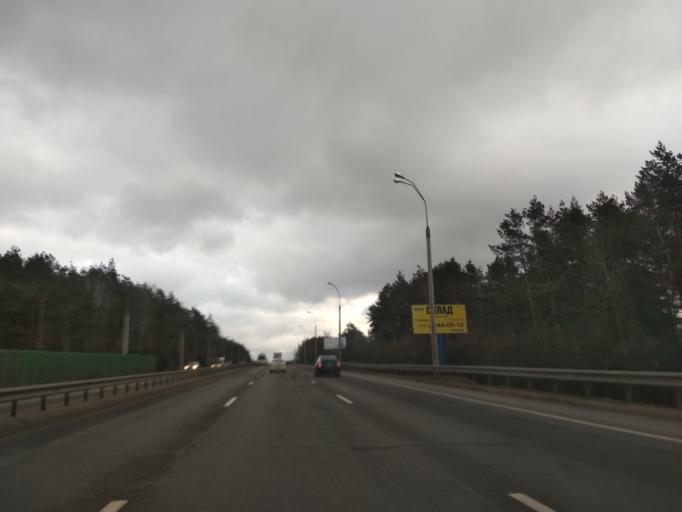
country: BY
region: Minsk
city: Vyaliki Trastsyanets
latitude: 53.8306
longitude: 27.7415
